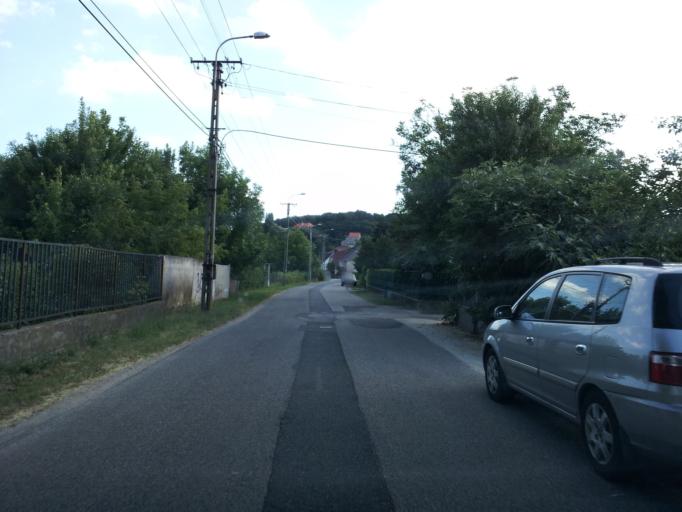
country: HU
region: Veszprem
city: Balatonalmadi
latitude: 47.0209
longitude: 18.0062
